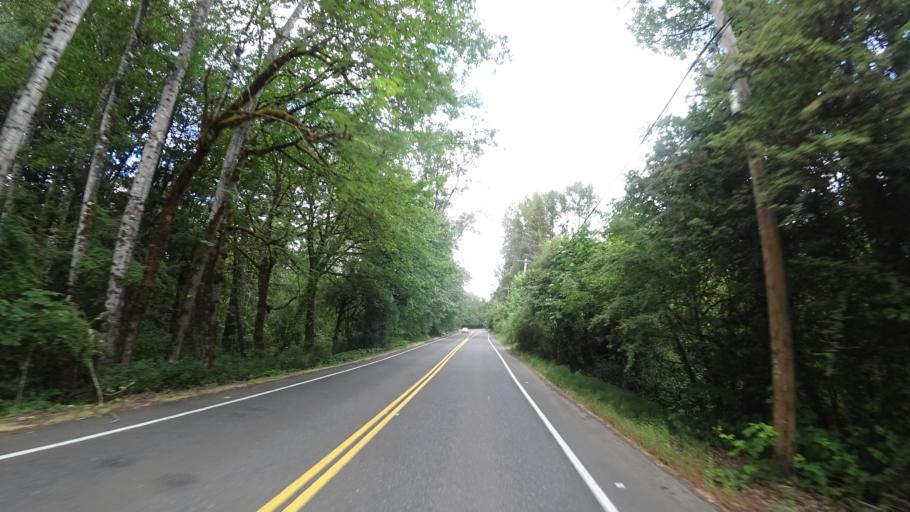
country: US
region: Oregon
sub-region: Clackamas County
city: Lake Oswego
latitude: 45.4410
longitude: -122.6709
